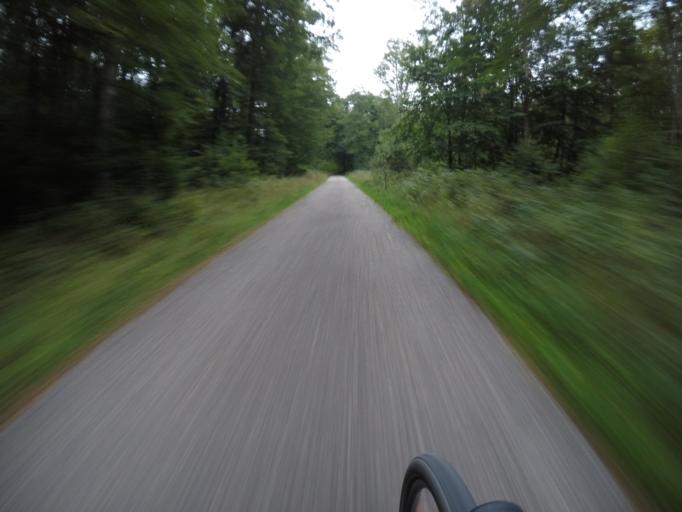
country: DE
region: Baden-Wuerttemberg
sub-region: Regierungsbezirk Stuttgart
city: Steinenbronn
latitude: 48.7087
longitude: 9.0966
